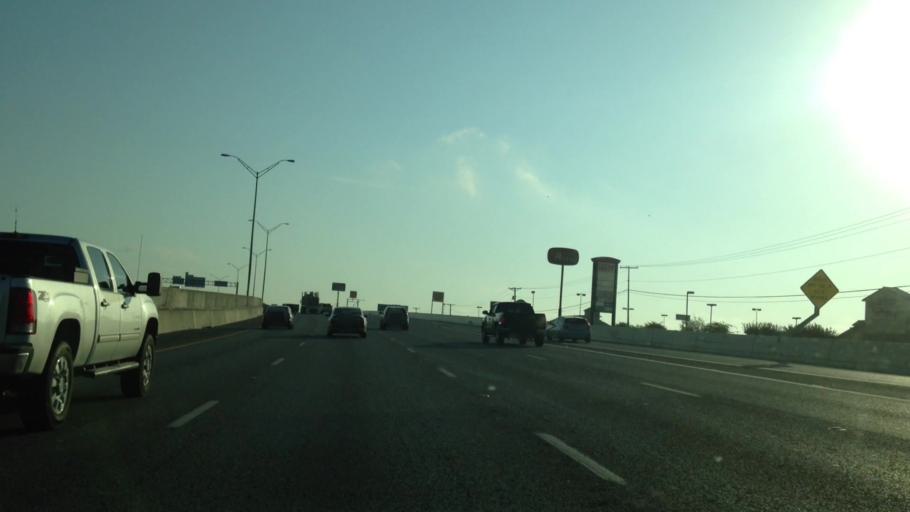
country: US
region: Texas
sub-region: Comal County
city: New Braunfels
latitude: 29.6962
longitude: -98.0974
